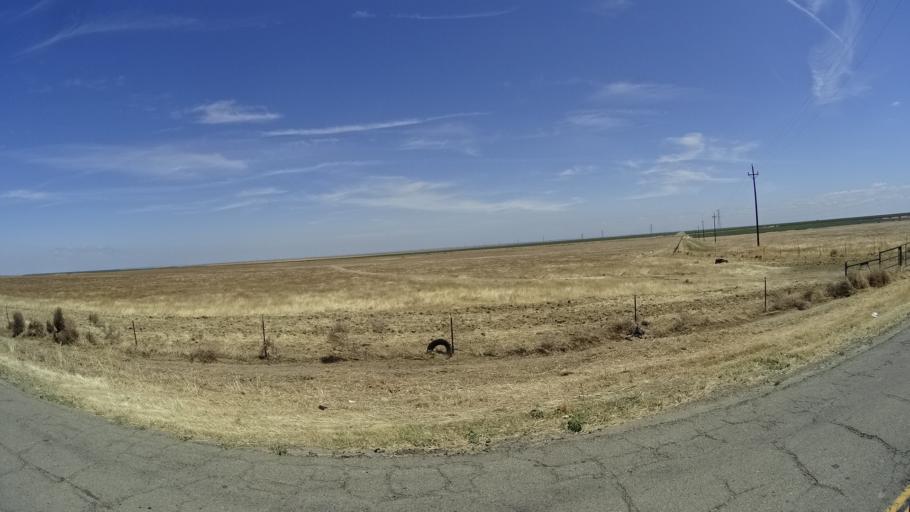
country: US
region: California
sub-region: Kings County
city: Kettleman City
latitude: 35.7892
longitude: -119.8887
